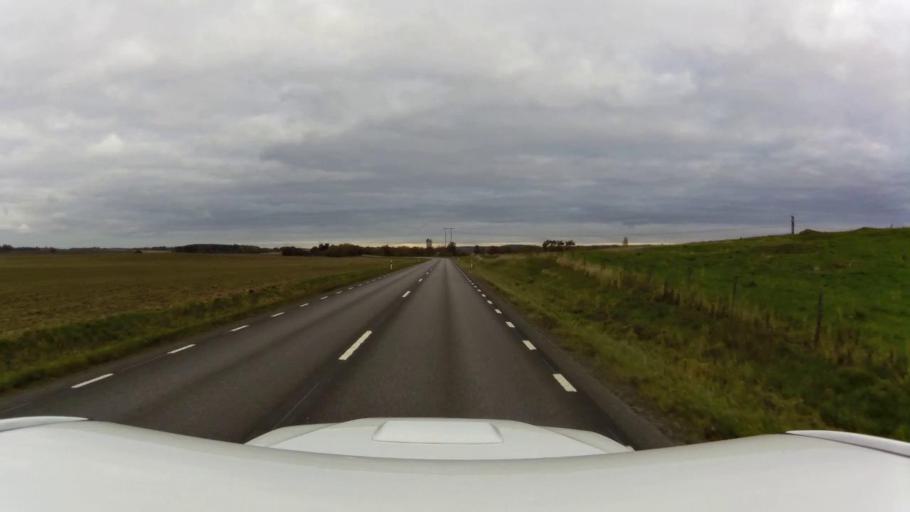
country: SE
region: OEstergoetland
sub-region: Linkopings Kommun
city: Ljungsbro
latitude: 58.5106
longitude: 15.4456
